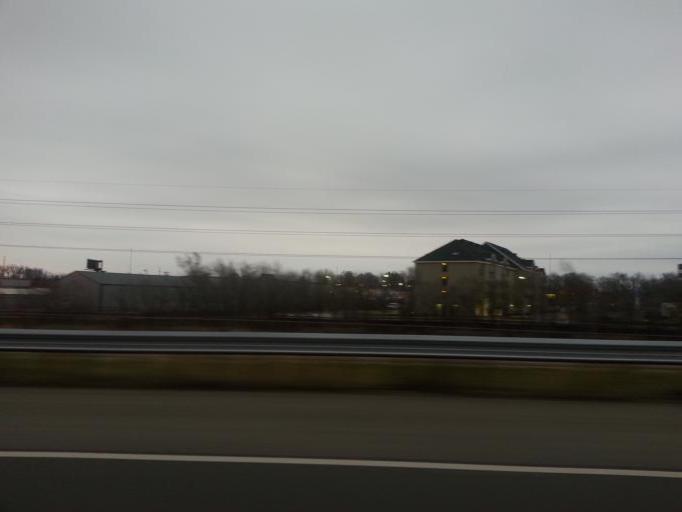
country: US
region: Iowa
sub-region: Linn County
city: Hiawatha
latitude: 42.0243
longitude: -91.6702
